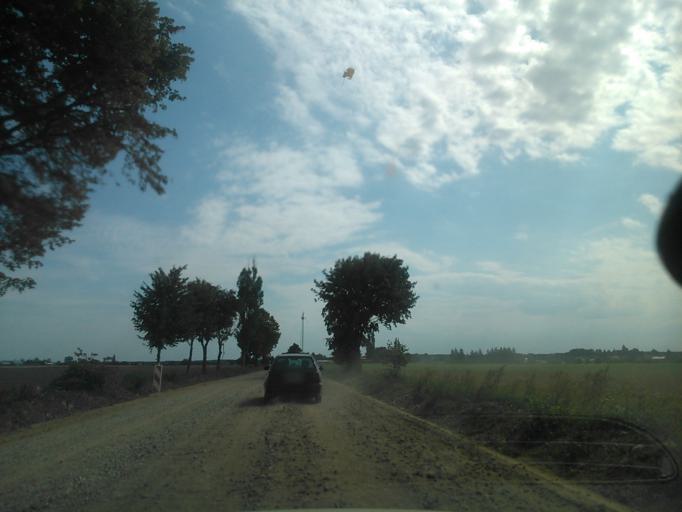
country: PL
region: Warmian-Masurian Voivodeship
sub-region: Powiat dzialdowski
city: Ilowo -Osada
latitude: 53.1831
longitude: 20.2896
